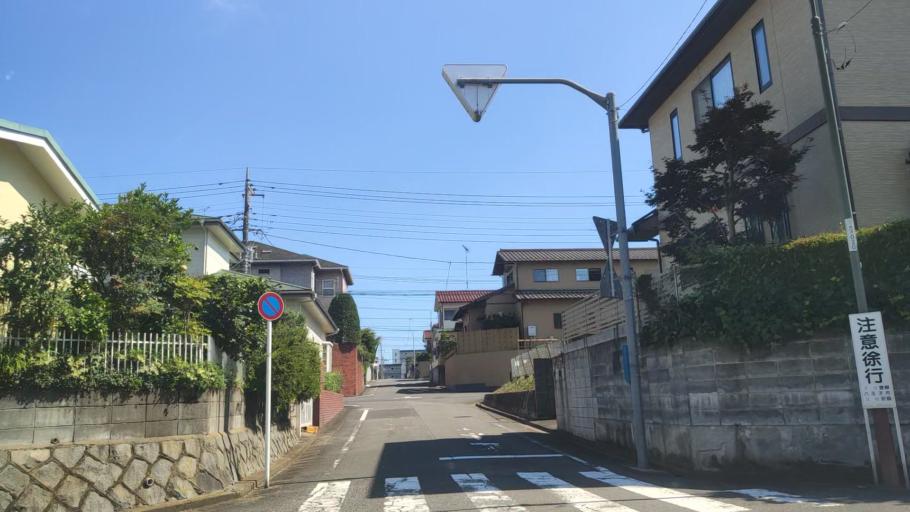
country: JP
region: Tokyo
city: Hachioji
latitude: 35.6461
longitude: 139.3073
